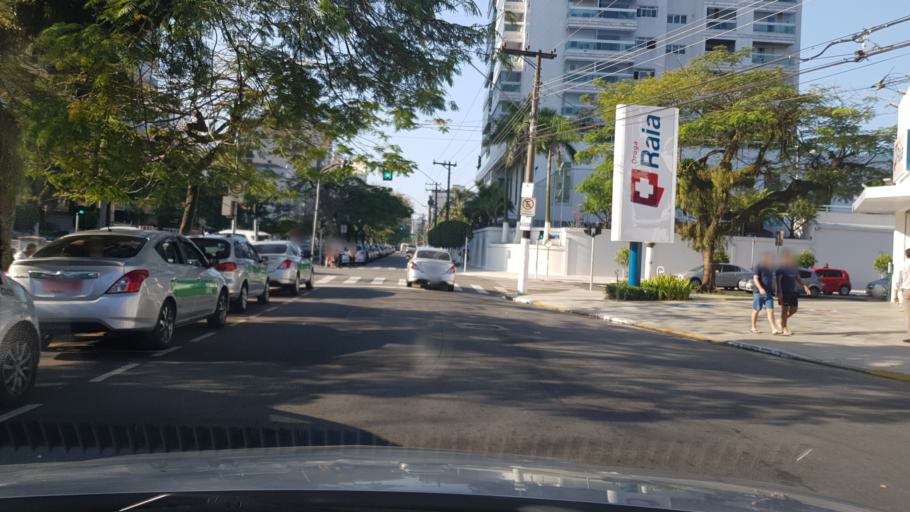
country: BR
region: Sao Paulo
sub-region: Santos
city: Santos
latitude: -23.9759
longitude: -46.3136
